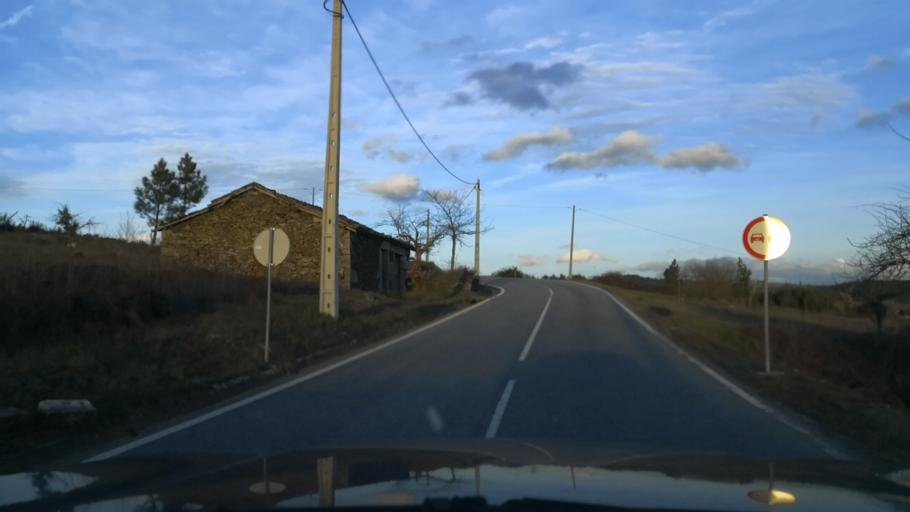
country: PT
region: Braganca
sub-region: Carrazeda de Ansiaes
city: Carrazeda de Anciaes
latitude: 41.2296
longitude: -7.3052
